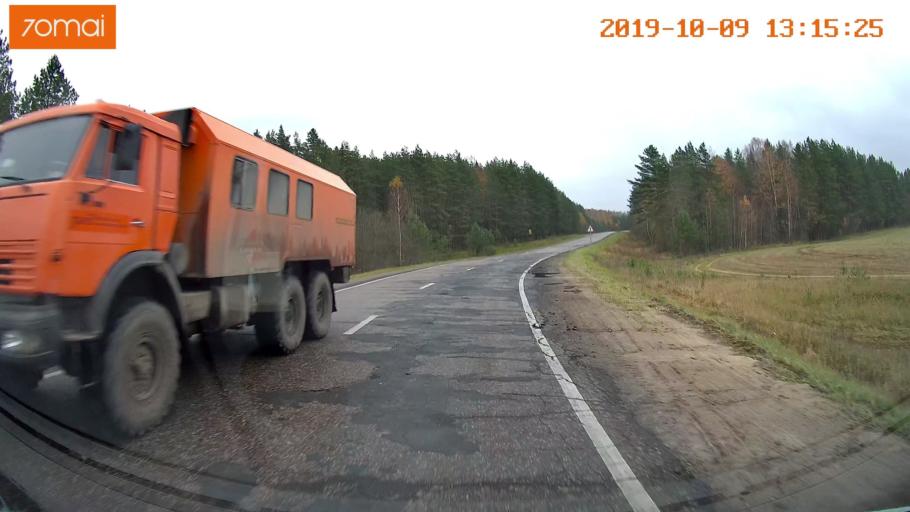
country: RU
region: Jaroslavl
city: Lyubim
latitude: 58.3675
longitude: 40.7519
